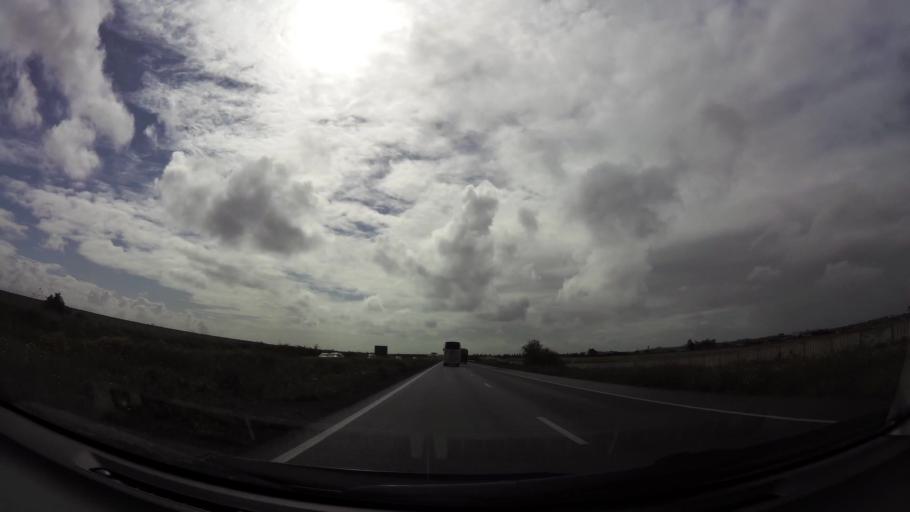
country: MA
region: Grand Casablanca
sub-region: Nouaceur
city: Dar Bouazza
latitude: 33.3536
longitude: -7.9669
